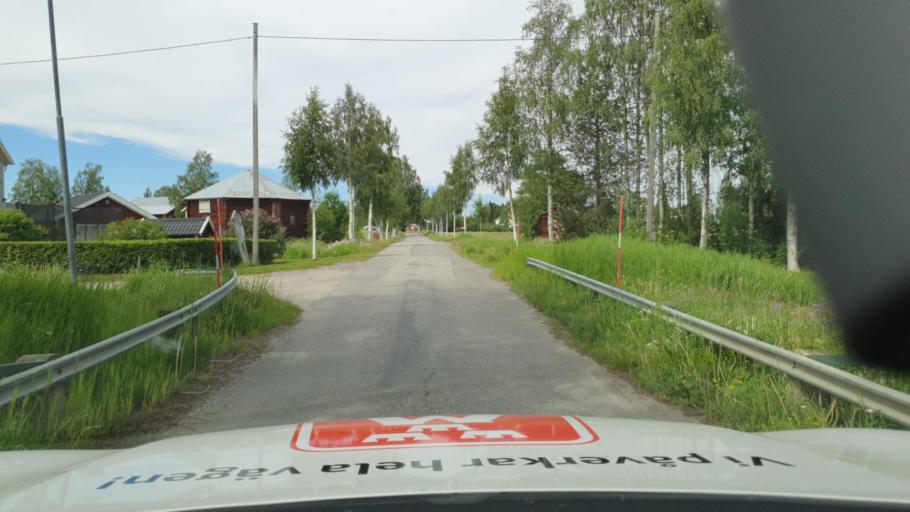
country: SE
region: Vaesterbotten
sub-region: Skelleftea Kommun
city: Burtraesk
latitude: 64.4527
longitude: 20.4807
